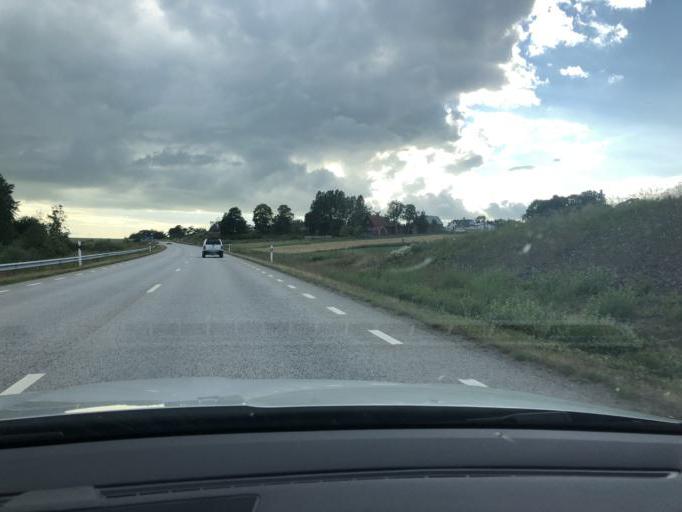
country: SE
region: Skane
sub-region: Simrishamns Kommun
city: Simrishamn
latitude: 55.5358
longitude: 14.2911
